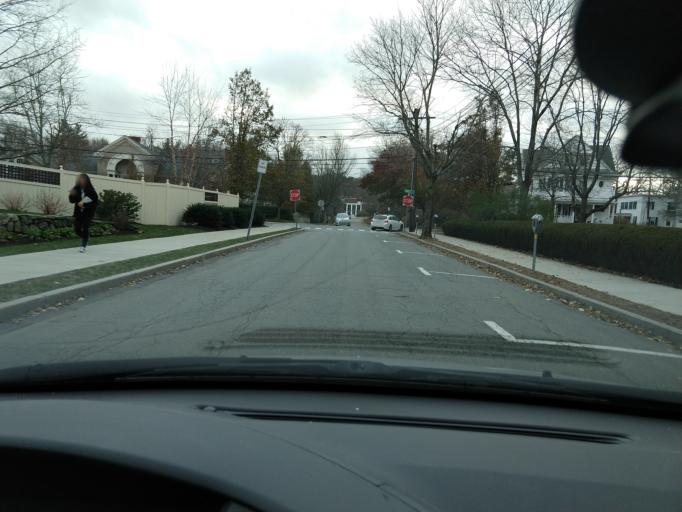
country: US
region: Massachusetts
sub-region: Middlesex County
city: Lexington
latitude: 42.4462
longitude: -71.2302
